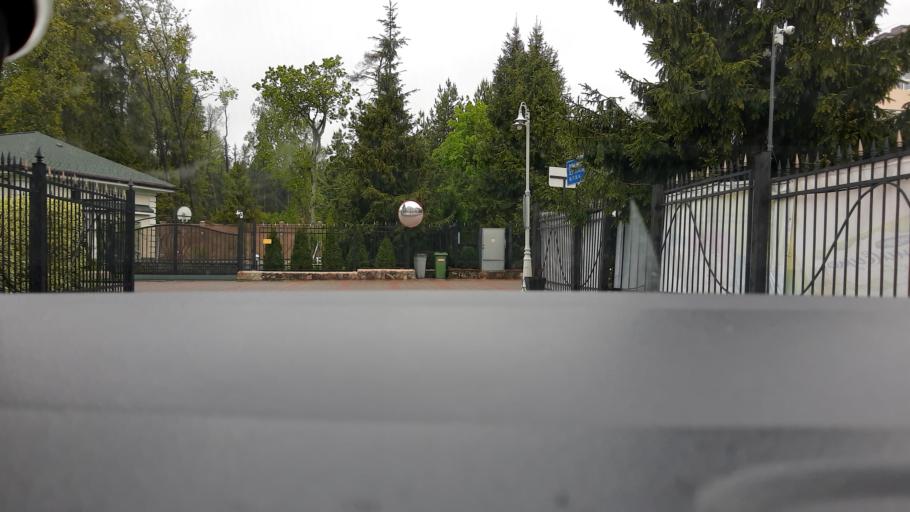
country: RU
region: Moskovskaya
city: Zhavoronki
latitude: 55.6747
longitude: 37.0786
